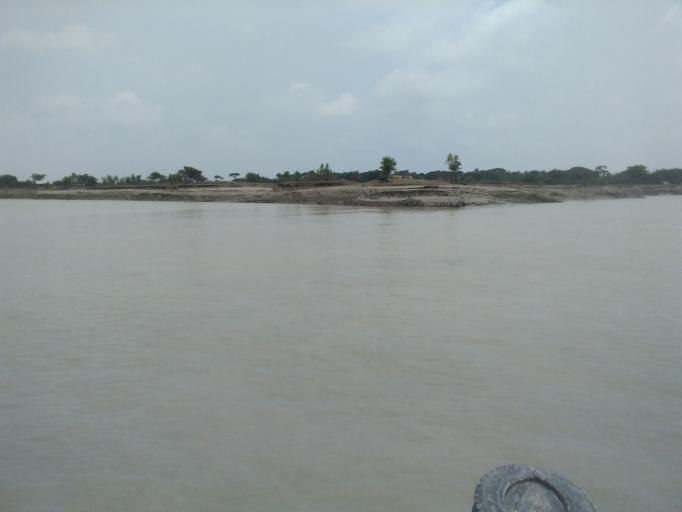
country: BD
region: Khulna
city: Phultala
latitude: 22.6450
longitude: 89.4109
